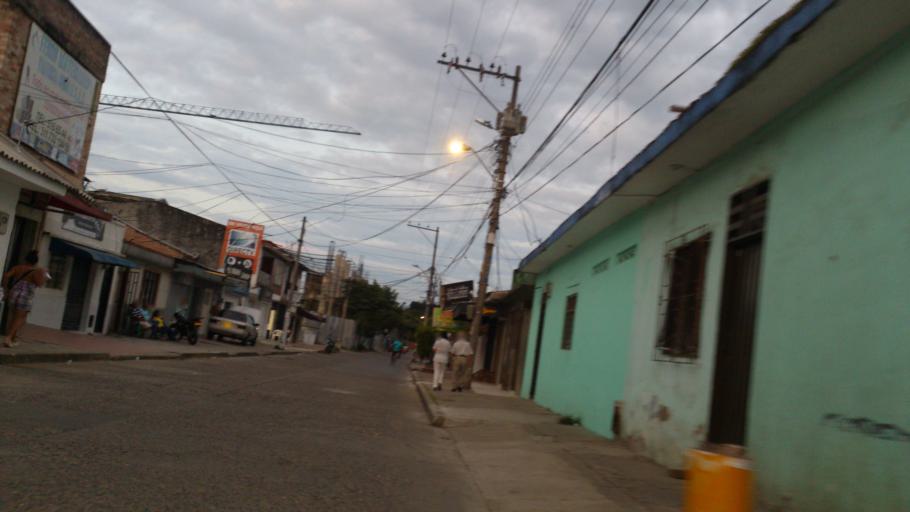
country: CO
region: Valle del Cauca
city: Jamundi
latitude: 3.2617
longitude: -76.5389
